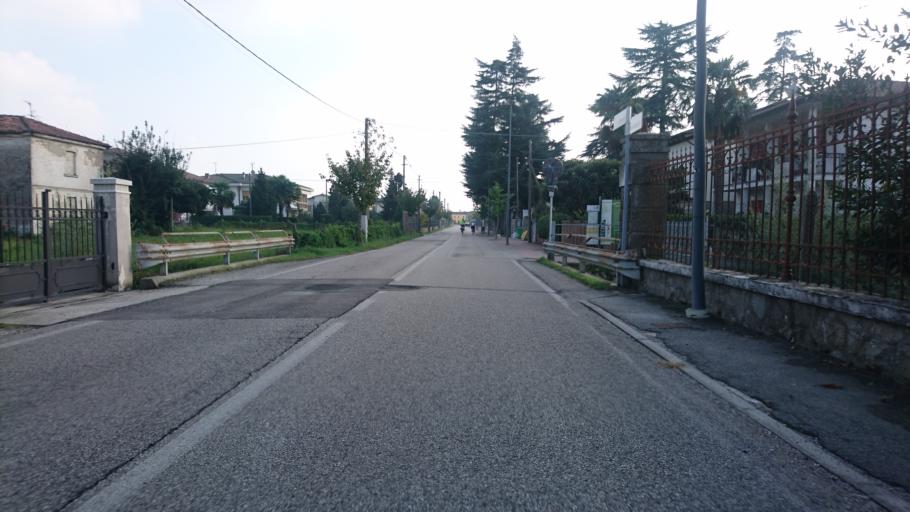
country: IT
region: Veneto
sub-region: Provincia di Rovigo
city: Arqua Polesine
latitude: 45.0072
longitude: 11.7410
